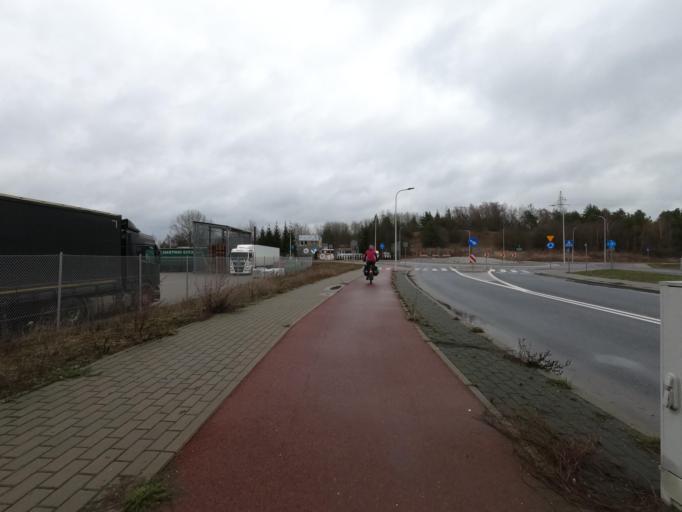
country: PL
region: Greater Poland Voivodeship
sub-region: Powiat pilski
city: Pila
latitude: 53.1422
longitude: 16.7802
